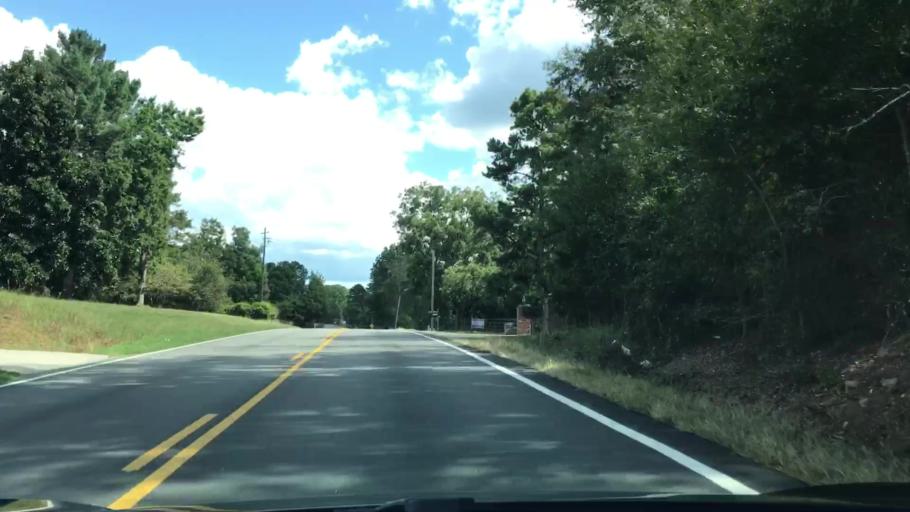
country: US
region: Georgia
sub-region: Greene County
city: Greensboro
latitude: 33.5681
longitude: -83.1612
